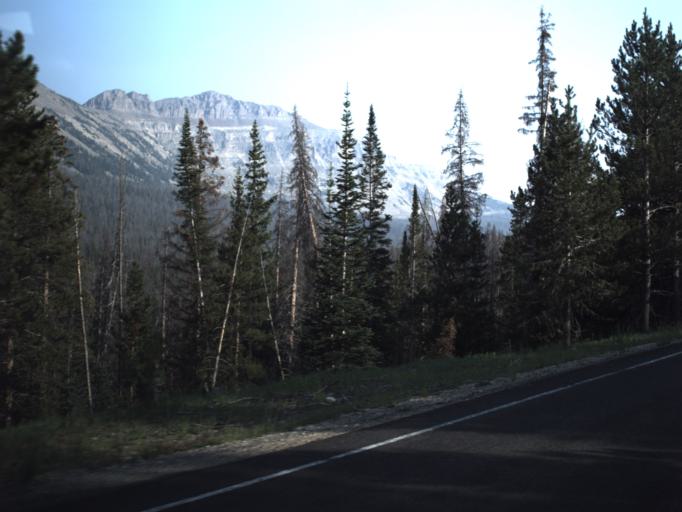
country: US
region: Utah
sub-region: Summit County
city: Kamas
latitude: 40.7577
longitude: -110.8803
